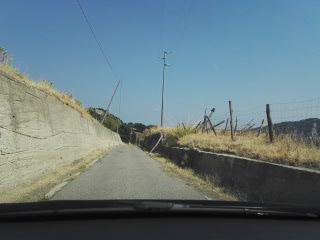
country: IT
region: Calabria
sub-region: Provincia di Reggio Calabria
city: Stilo
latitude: 38.4499
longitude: 16.4631
